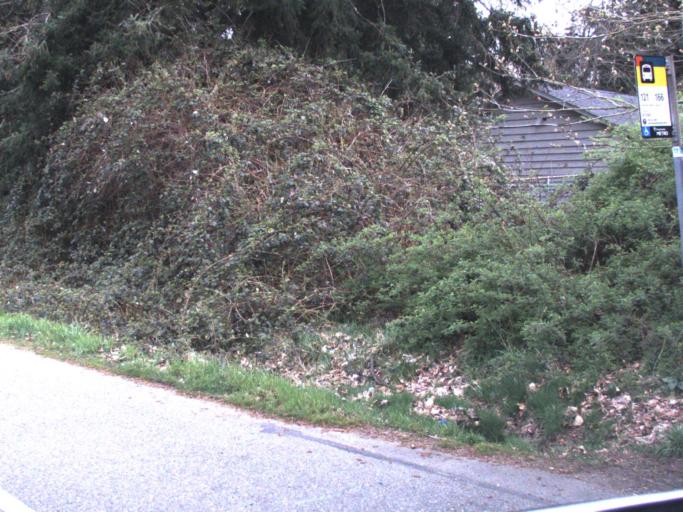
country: US
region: Washington
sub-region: King County
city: Normandy Park
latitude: 47.4370
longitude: -122.3350
